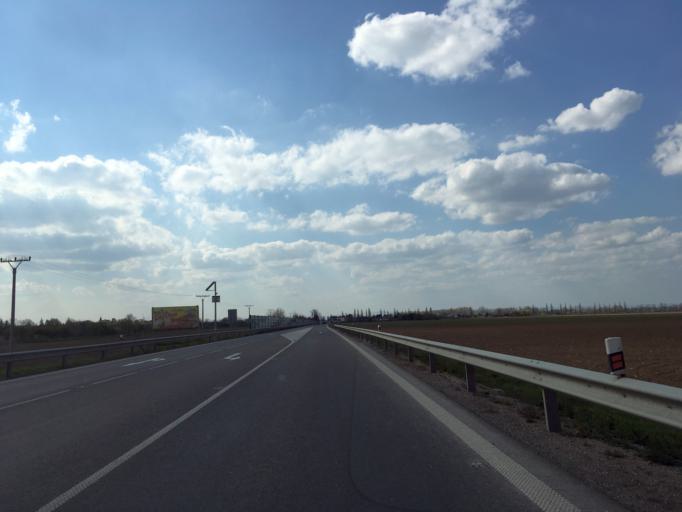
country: SK
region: Trnavsky
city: Sladkovicovo
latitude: 48.2050
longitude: 17.6603
